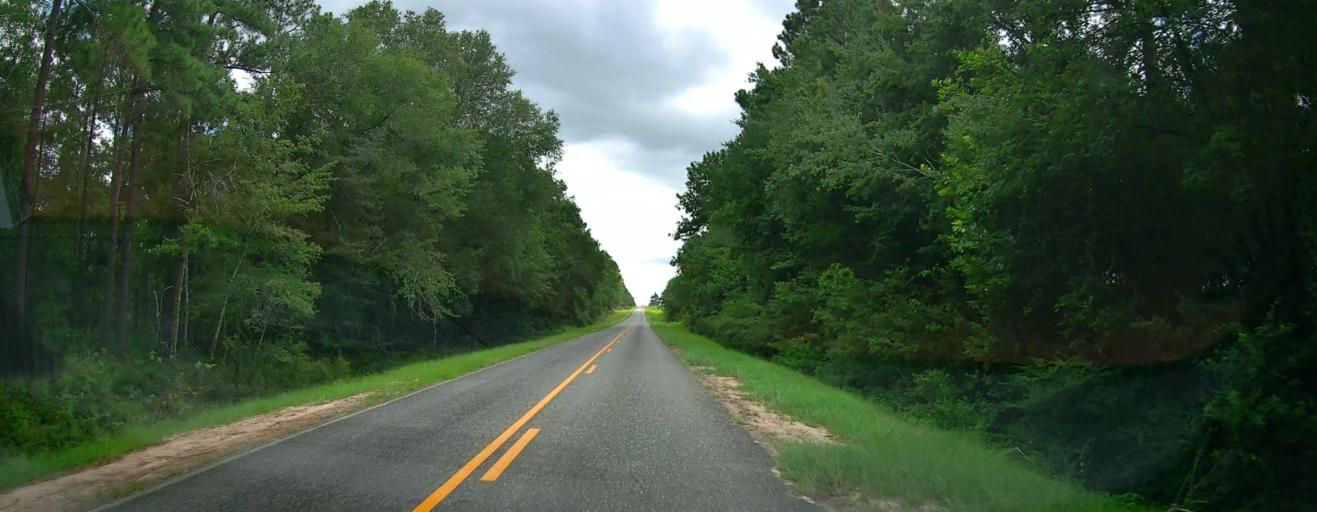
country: US
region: Georgia
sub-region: Turner County
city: Ashburn
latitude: 31.7192
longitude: -83.5056
